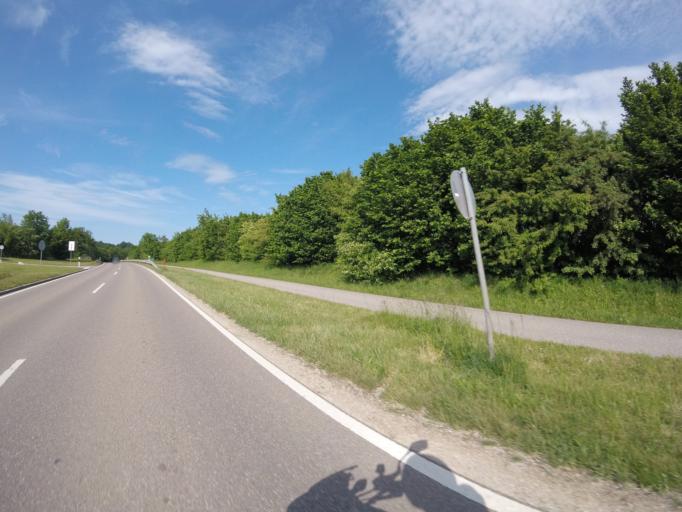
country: DE
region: Bavaria
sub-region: Upper Bavaria
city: Reichertshausen
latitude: 48.4584
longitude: 11.4941
